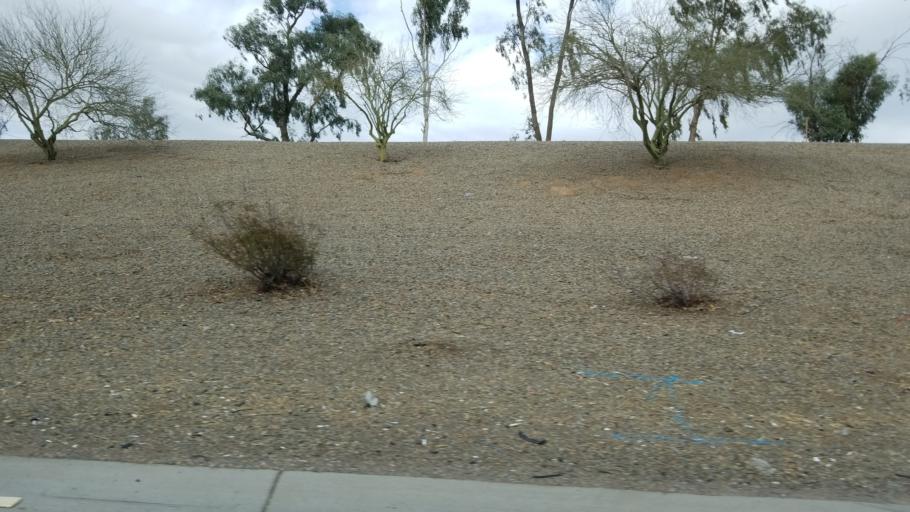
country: US
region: Arizona
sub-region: Maricopa County
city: Tolleson
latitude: 33.4629
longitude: -112.2145
